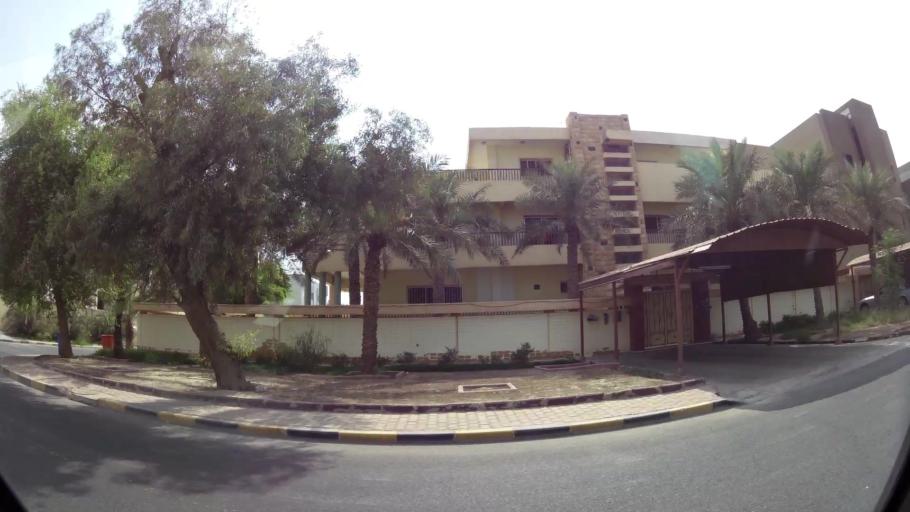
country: KW
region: Al Asimah
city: Kuwait City
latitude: 29.3571
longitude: 47.9795
